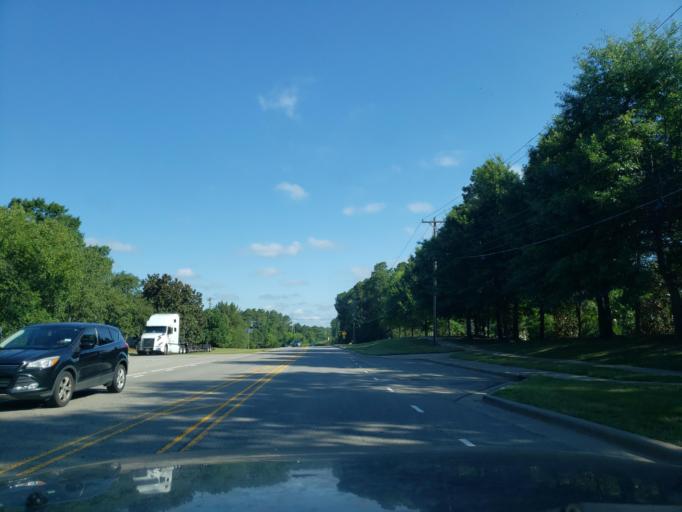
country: US
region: North Carolina
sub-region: Durham County
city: Durham
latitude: 35.9410
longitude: -78.8649
